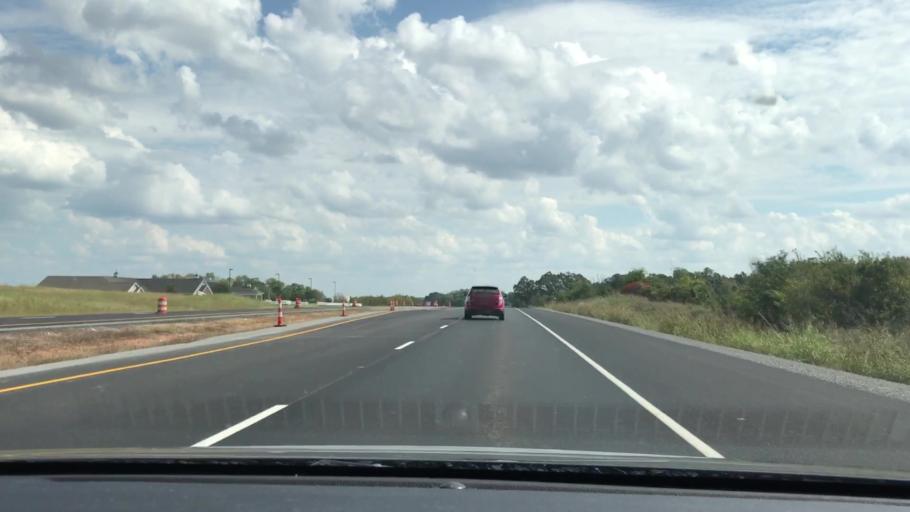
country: US
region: Kentucky
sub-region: Trigg County
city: Cadiz
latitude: 36.8602
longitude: -87.8066
